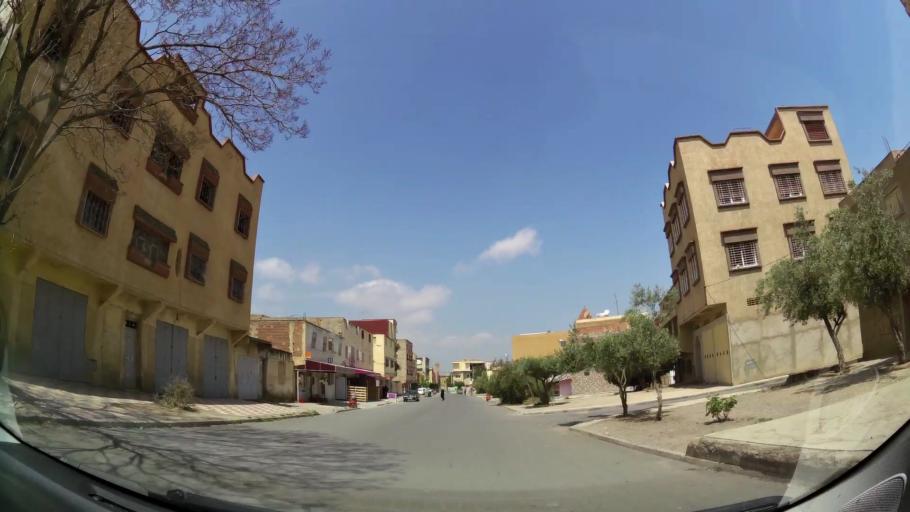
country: MA
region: Oriental
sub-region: Oujda-Angad
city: Oujda
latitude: 34.6859
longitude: -1.8859
